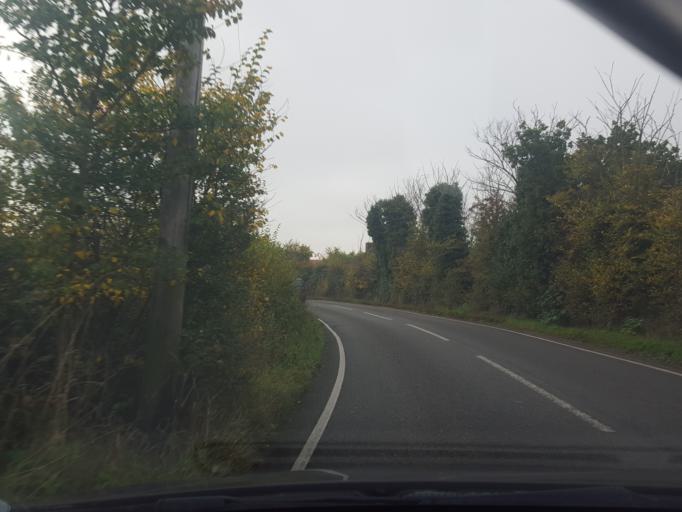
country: GB
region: England
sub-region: Essex
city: Little Clacton
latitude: 51.8092
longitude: 1.1262
